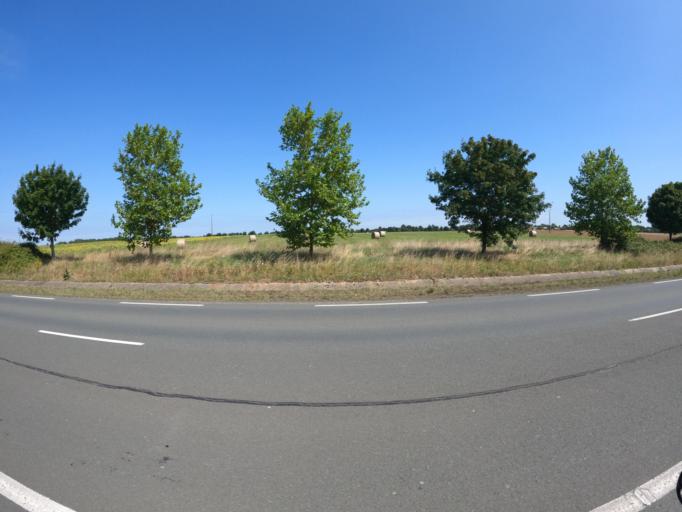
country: FR
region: Poitou-Charentes
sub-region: Departement des Deux-Sevres
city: Vouille
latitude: 46.3022
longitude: -0.3526
